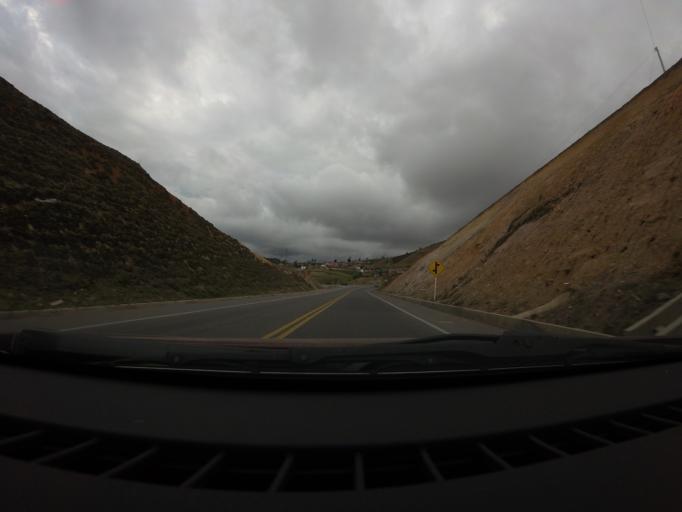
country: CO
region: Boyaca
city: Tunja
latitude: 5.5004
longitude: -73.3792
